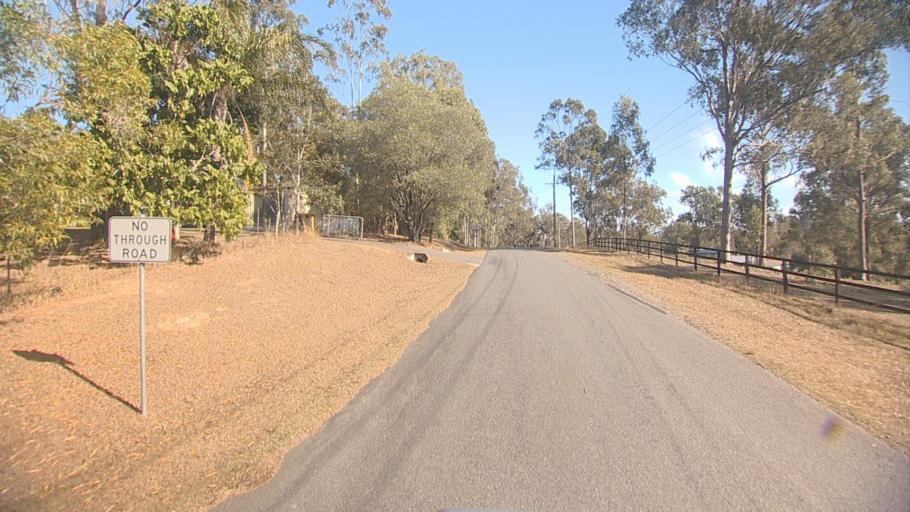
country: AU
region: Queensland
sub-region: Logan
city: Cedar Vale
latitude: -27.8500
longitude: 152.9913
